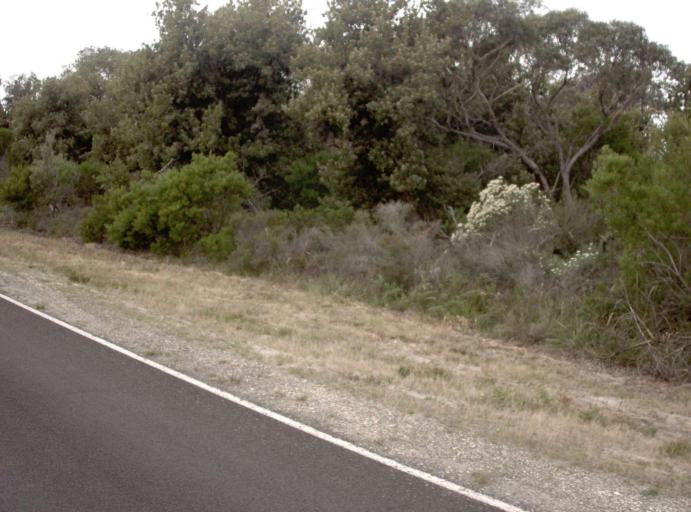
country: AU
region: Victoria
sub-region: East Gippsland
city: Bairnsdale
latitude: -38.0943
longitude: 147.5143
